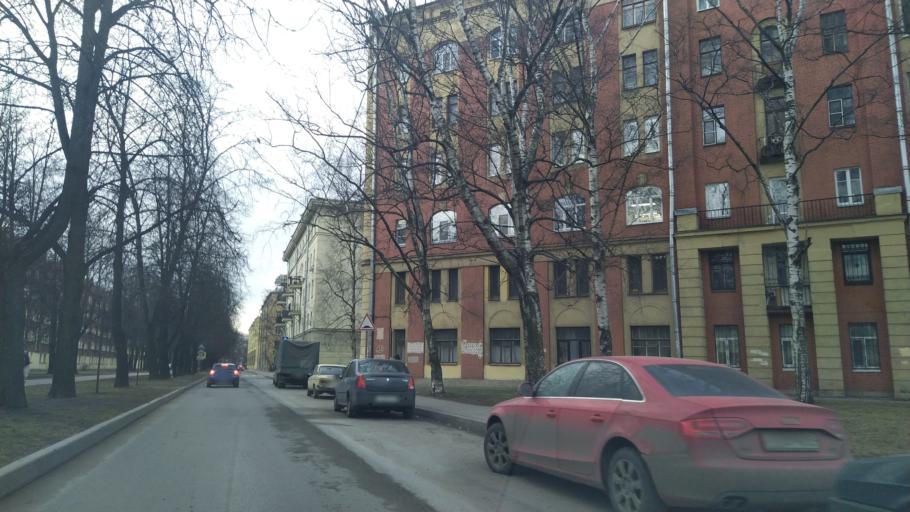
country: RU
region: Leningrad
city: Sampsonievskiy
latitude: 59.9809
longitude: 30.3496
